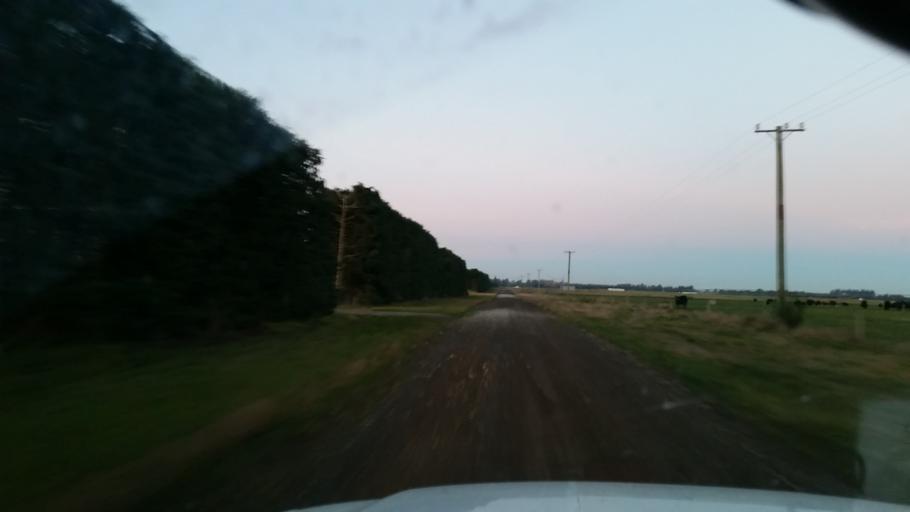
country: NZ
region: Canterbury
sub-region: Ashburton District
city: Tinwald
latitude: -43.9344
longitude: 171.5896
